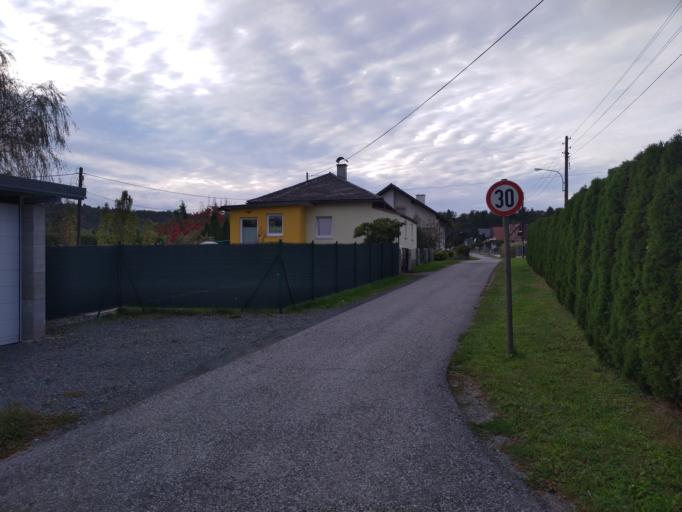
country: AT
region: Styria
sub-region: Politischer Bezirk Leibnitz
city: Grossklein
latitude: 46.7470
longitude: 15.4347
